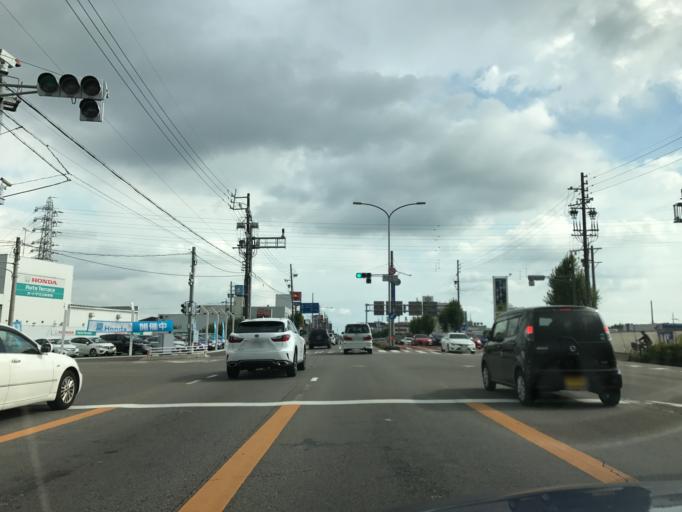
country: JP
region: Gifu
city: Gifu-shi
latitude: 35.4112
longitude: 136.7851
